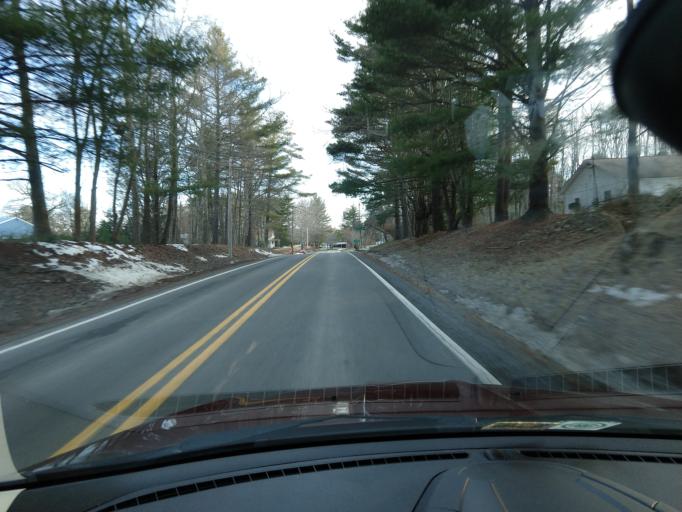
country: US
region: West Virginia
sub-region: Pocahontas County
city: Marlinton
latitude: 38.0720
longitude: -80.2880
